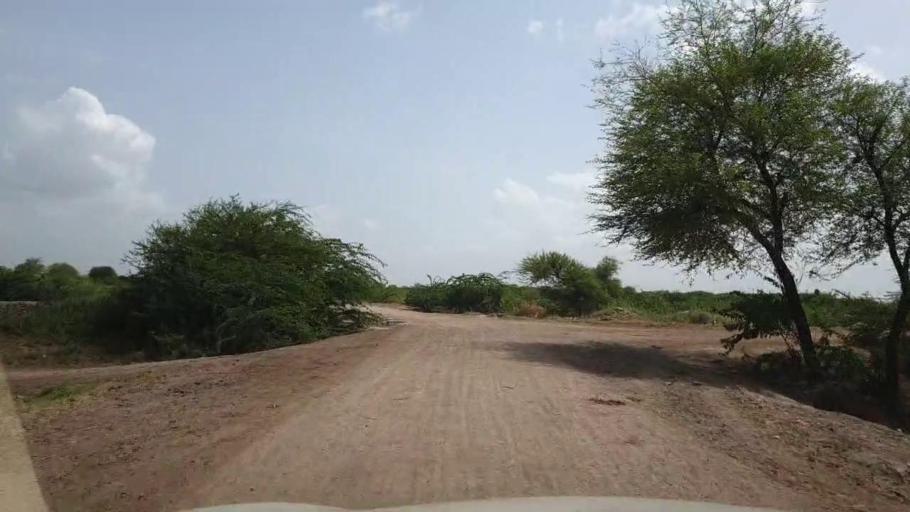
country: PK
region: Sindh
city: Kadhan
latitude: 24.3960
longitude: 68.7963
